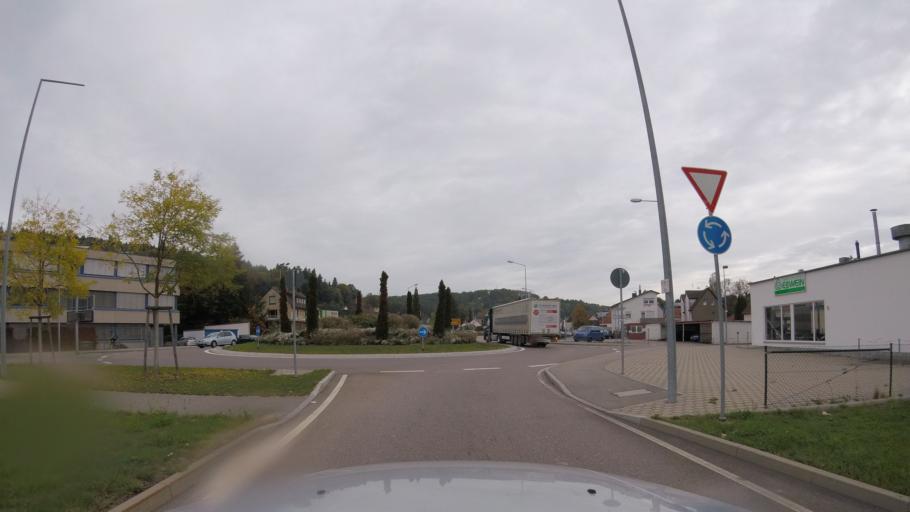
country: DE
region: Baden-Wuerttemberg
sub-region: Regierungsbezirk Stuttgart
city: Schwabisch Gmund
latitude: 48.7971
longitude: 9.7827
